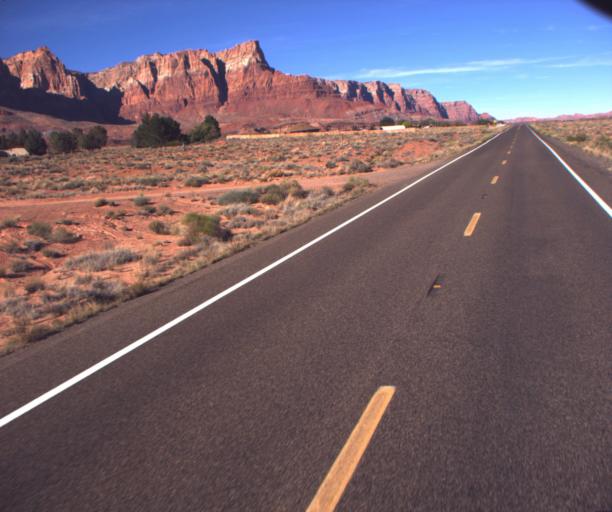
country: US
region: Arizona
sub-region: Coconino County
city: Page
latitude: 36.7849
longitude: -111.6867
